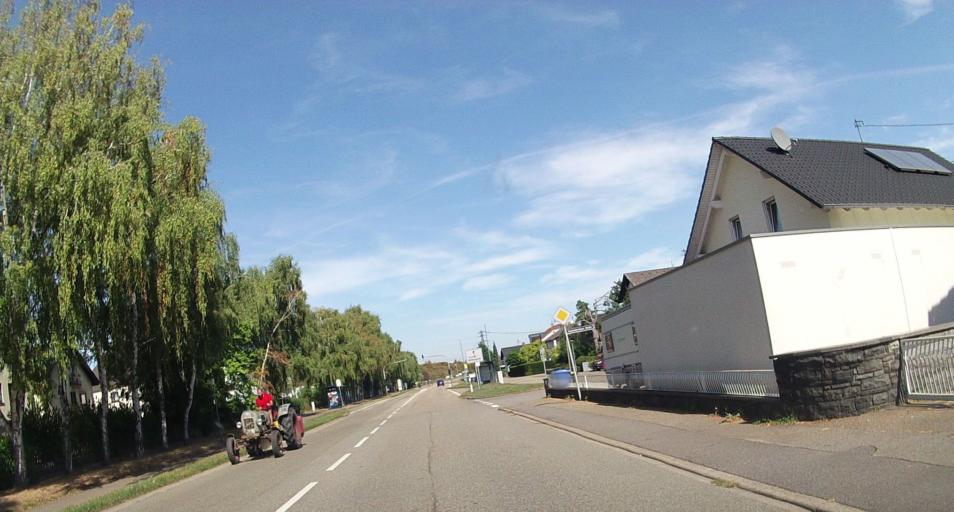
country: DE
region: Baden-Wuerttemberg
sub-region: Karlsruhe Region
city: Rastatt
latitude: 48.8129
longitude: 8.1955
